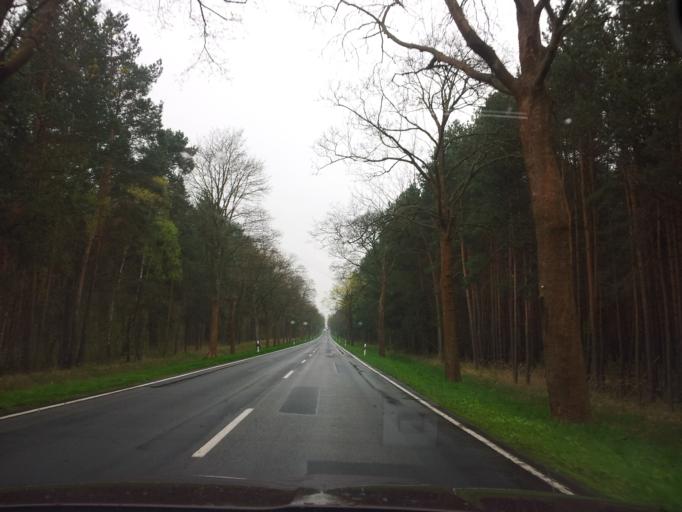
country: DE
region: Brandenburg
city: Treuenbrietzen
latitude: 52.0603
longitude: 12.8246
